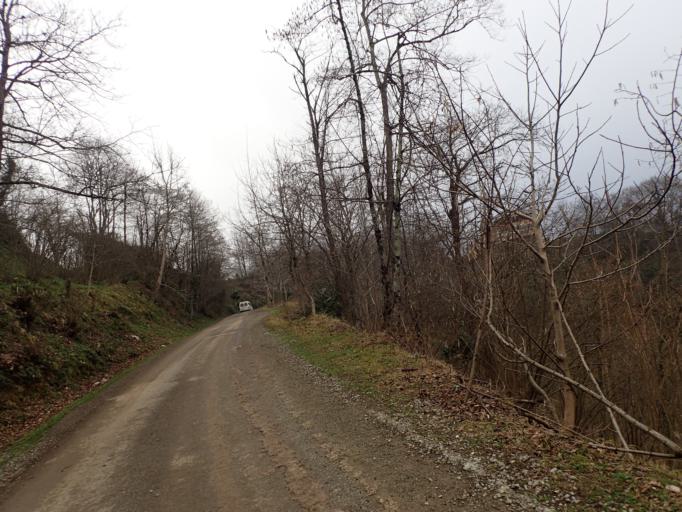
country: TR
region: Ordu
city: Camas
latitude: 40.9189
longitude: 37.5644
